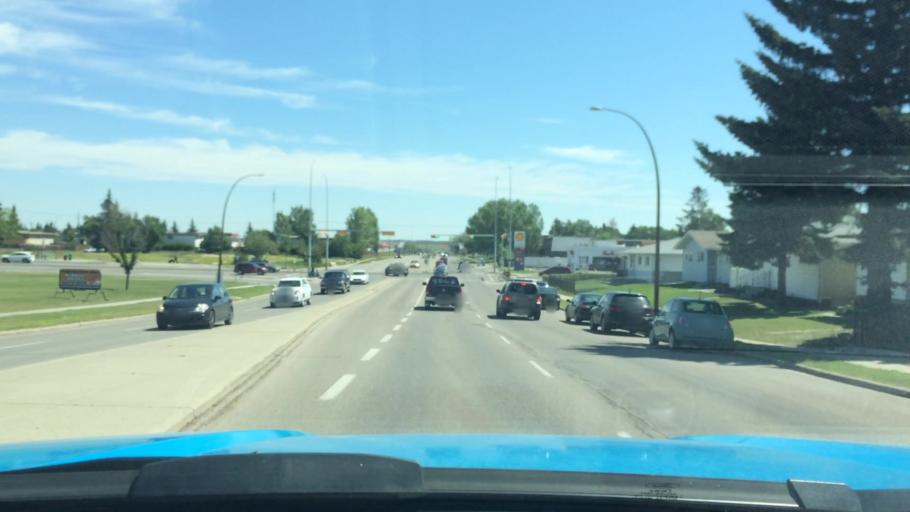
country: CA
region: Alberta
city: Calgary
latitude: 51.1106
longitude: -114.0643
